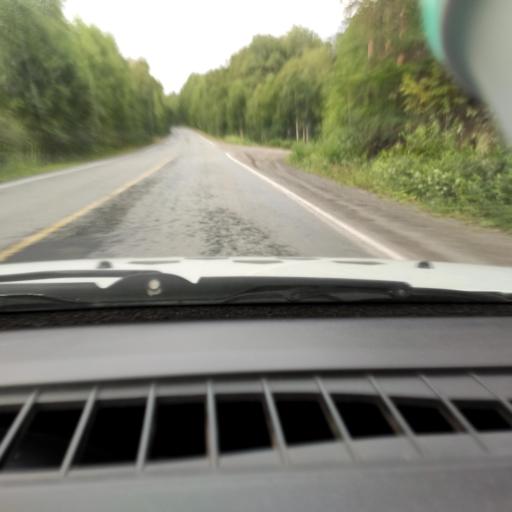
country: RU
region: Chelyabinsk
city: Karabash
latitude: 55.5435
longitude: 60.3546
